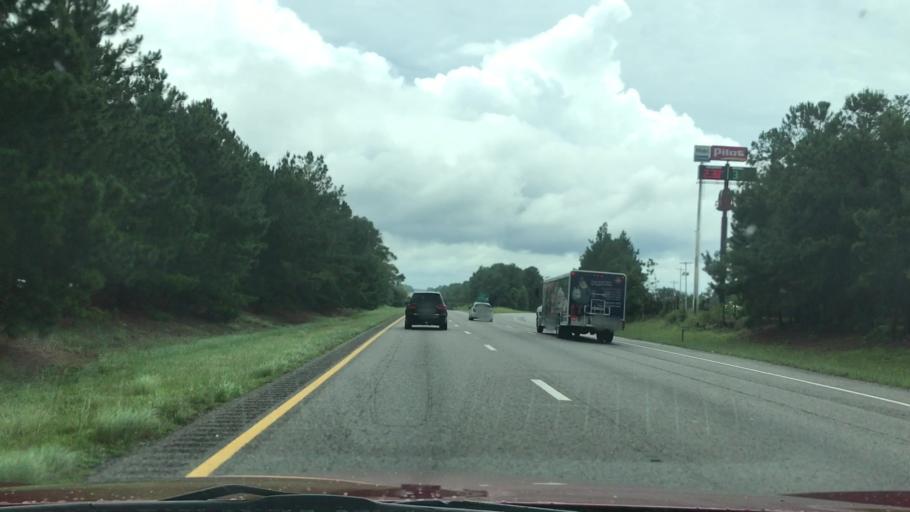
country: US
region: South Carolina
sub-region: Calhoun County
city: Saint Matthews
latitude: 33.6374
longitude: -80.8774
